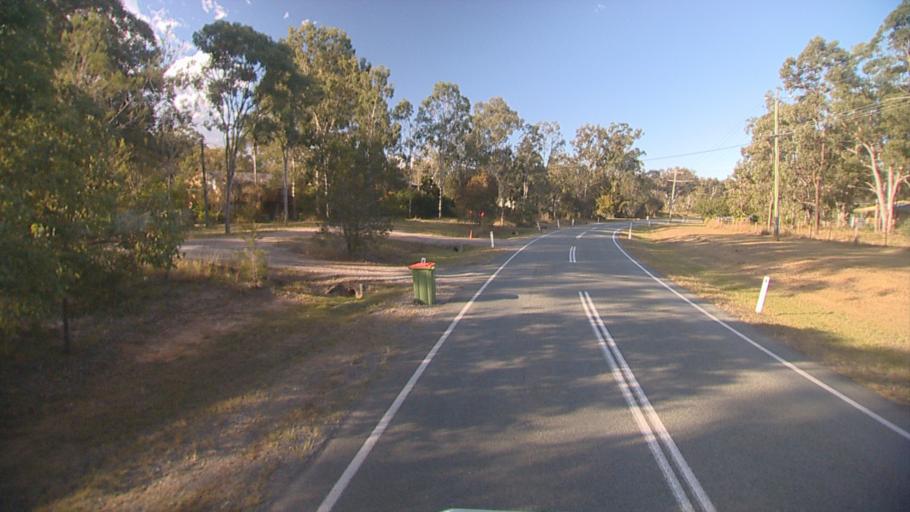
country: AU
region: Queensland
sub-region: Logan
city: Park Ridge South
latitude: -27.7173
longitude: 152.9717
